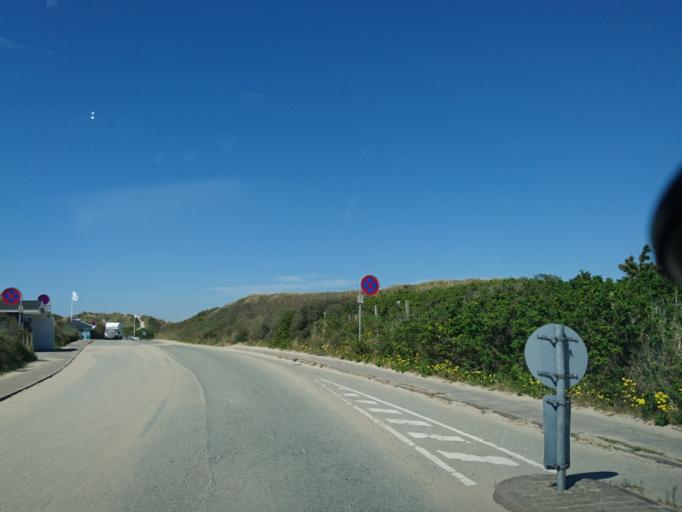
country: DK
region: North Denmark
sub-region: Hjorring Kommune
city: Sindal
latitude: 57.5949
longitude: 10.1841
